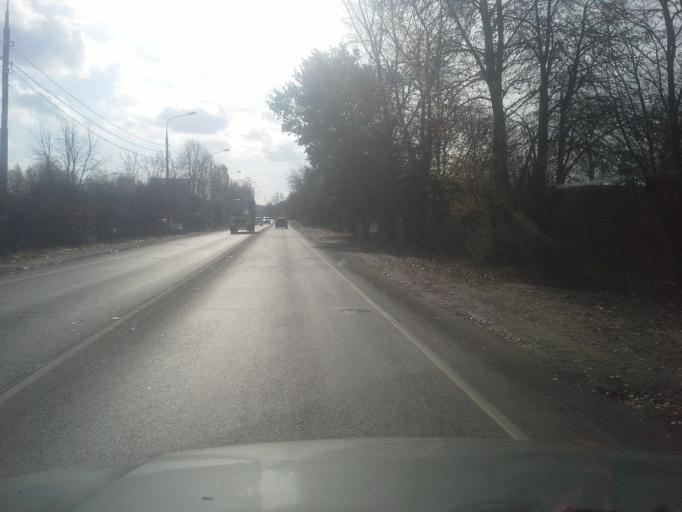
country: RU
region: Moskovskaya
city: Zvenigorod
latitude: 55.7255
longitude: 36.8621
